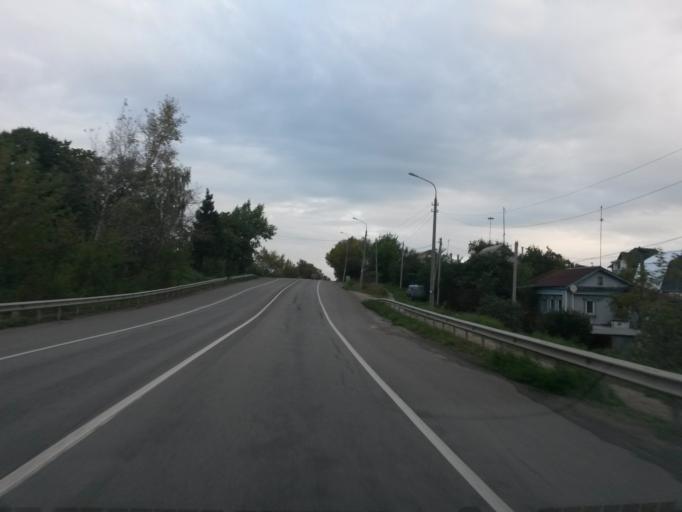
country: RU
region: Moskovskaya
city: Stolbovaya
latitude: 55.2758
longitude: 37.5099
